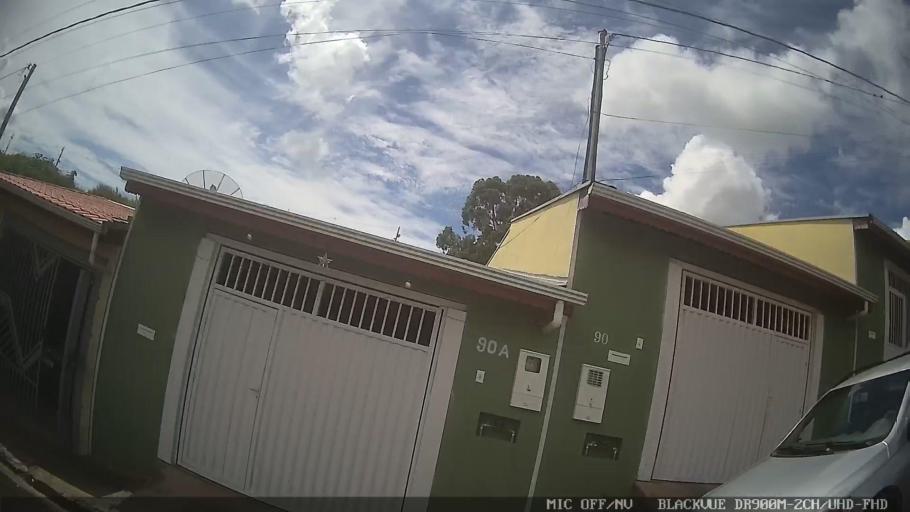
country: BR
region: Minas Gerais
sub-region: Extrema
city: Extrema
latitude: -22.7381
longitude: -46.3794
